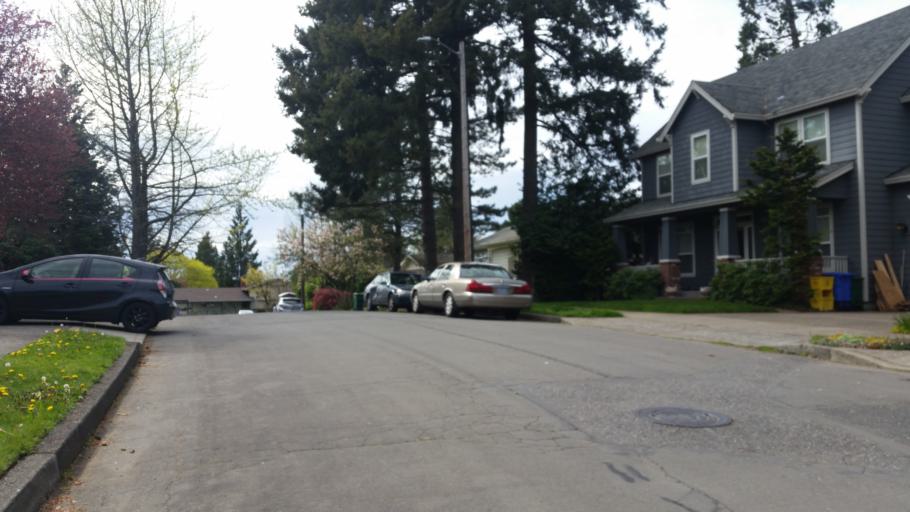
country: US
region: Oregon
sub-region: Washington County
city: Garden Home-Whitford
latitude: 45.4749
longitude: -122.7087
